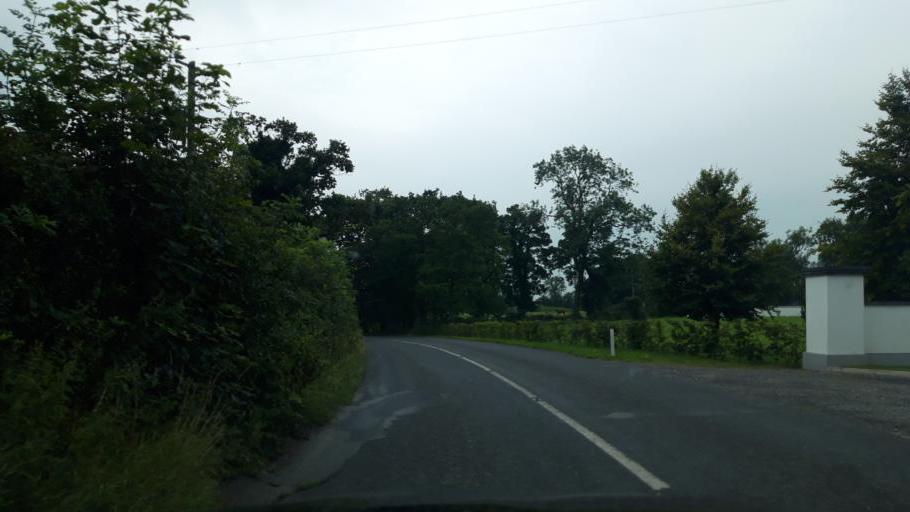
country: IE
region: Munster
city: Fethard
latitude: 52.5428
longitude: -7.6816
